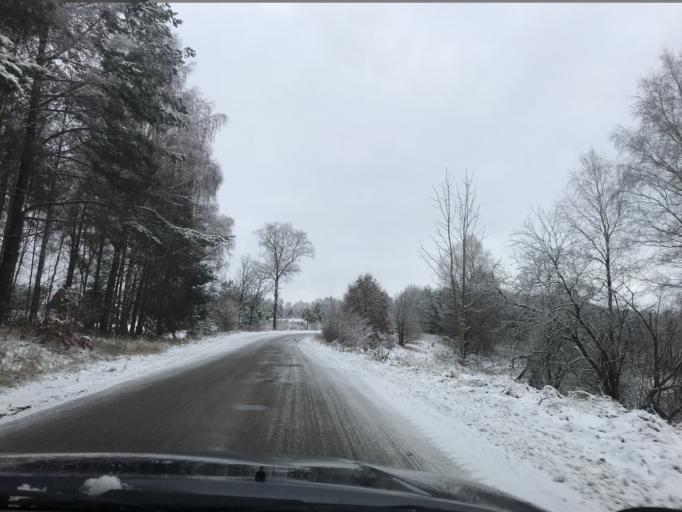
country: PL
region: Pomeranian Voivodeship
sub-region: Powiat bytowski
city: Parchowo
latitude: 54.2308
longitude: 17.5719
